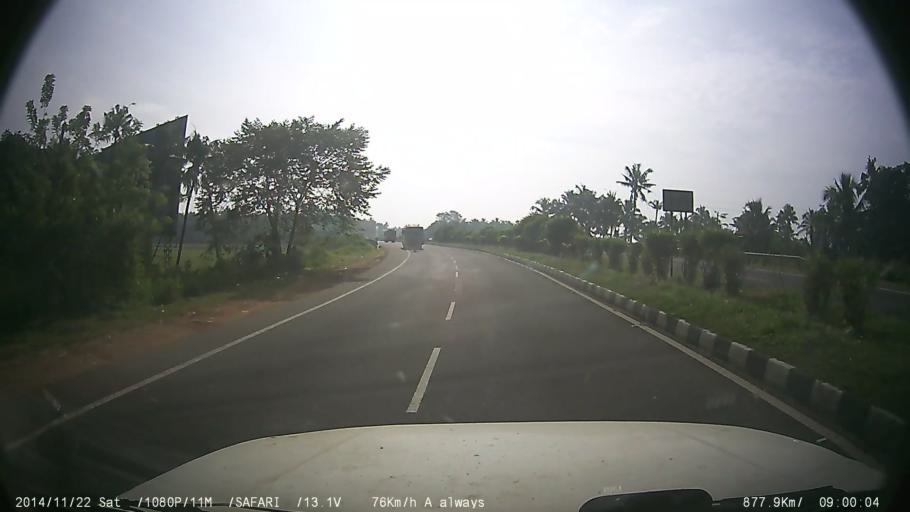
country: IN
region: Kerala
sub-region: Thrissur District
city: Irinjalakuda
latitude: 10.3842
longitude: 76.2921
